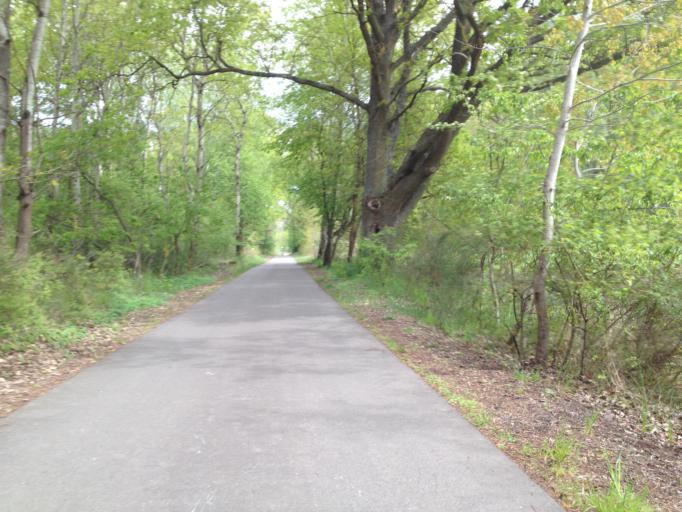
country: DE
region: Brandenburg
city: Lychen
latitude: 53.2328
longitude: 13.2829
